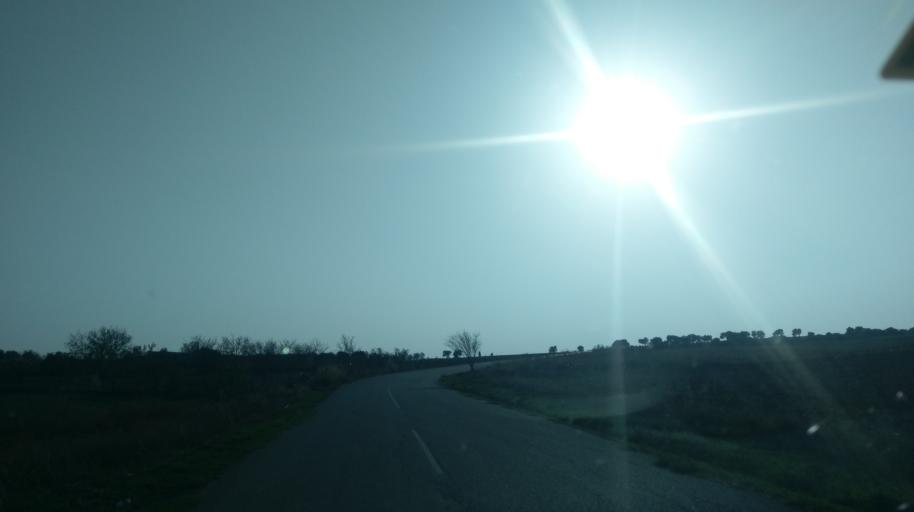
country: CY
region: Ammochostos
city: Leonarisso
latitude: 35.4396
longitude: 34.0876
